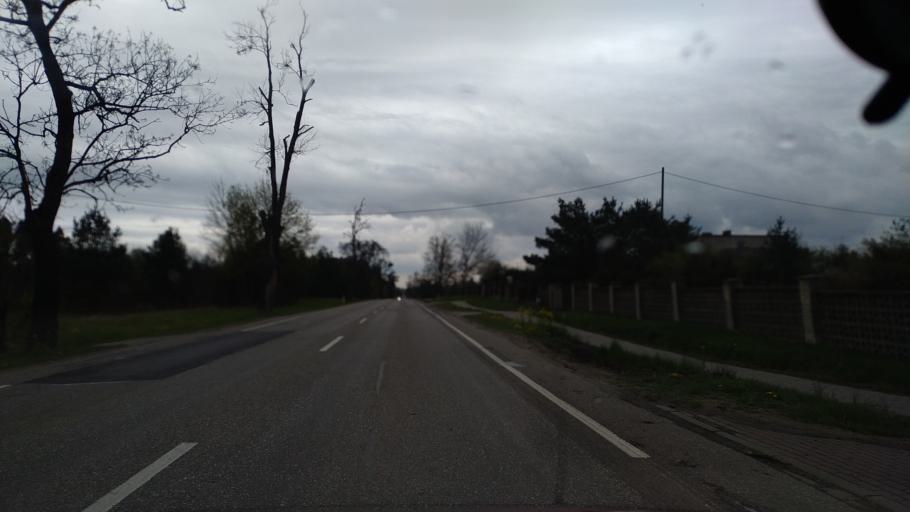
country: PL
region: Pomeranian Voivodeship
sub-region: Powiat tczewski
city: Pelplin
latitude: 54.0273
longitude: 18.6441
